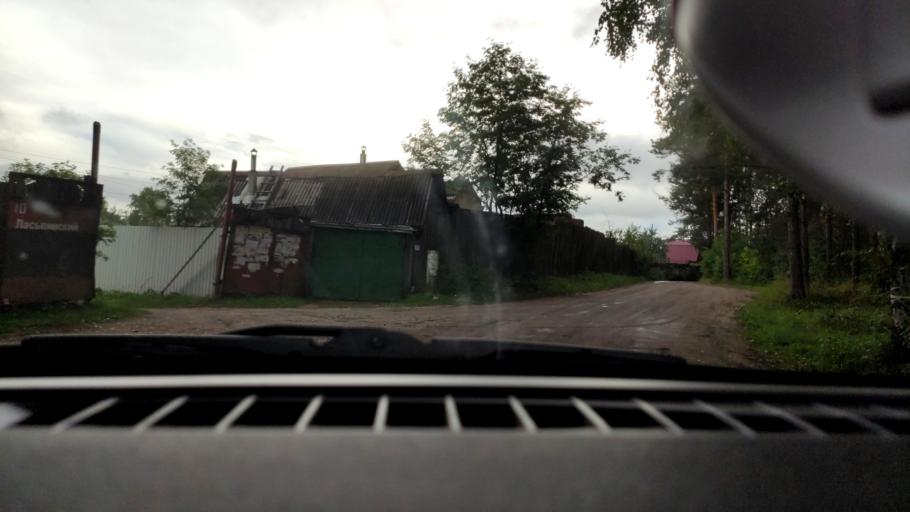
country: RU
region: Perm
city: Overyata
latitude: 58.0524
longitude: 55.9791
